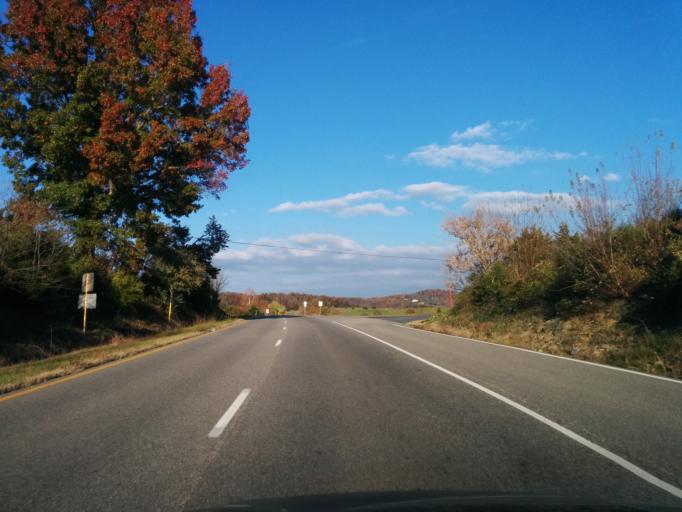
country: US
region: Virginia
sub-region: Rockbridge County
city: East Lexington
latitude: 37.8059
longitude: -79.4037
